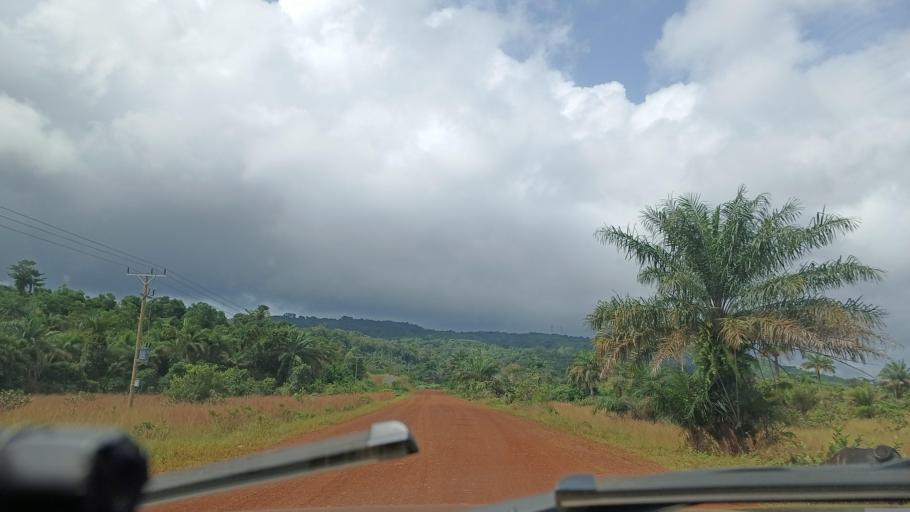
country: LR
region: Grand Cape Mount
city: Robertsport
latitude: 6.7486
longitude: -11.3472
